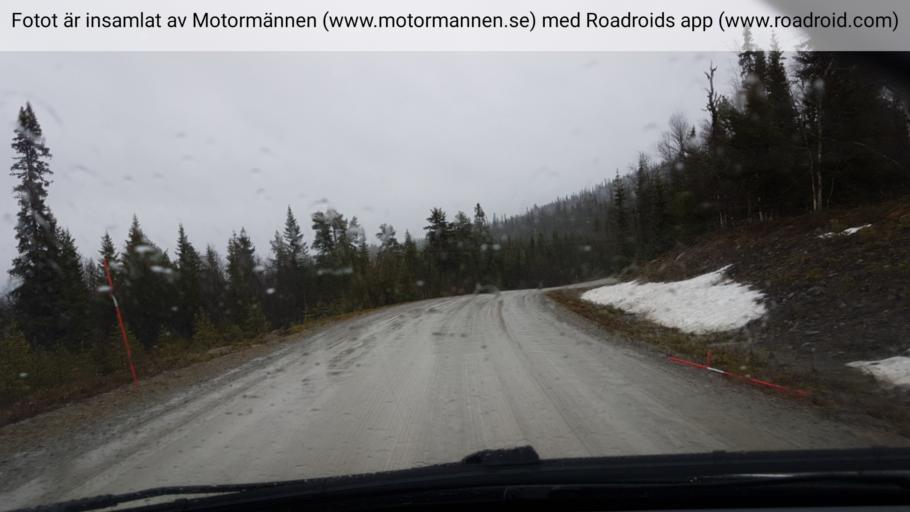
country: SE
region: Jaemtland
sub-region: Are Kommun
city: Are
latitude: 62.6421
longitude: 13.0709
